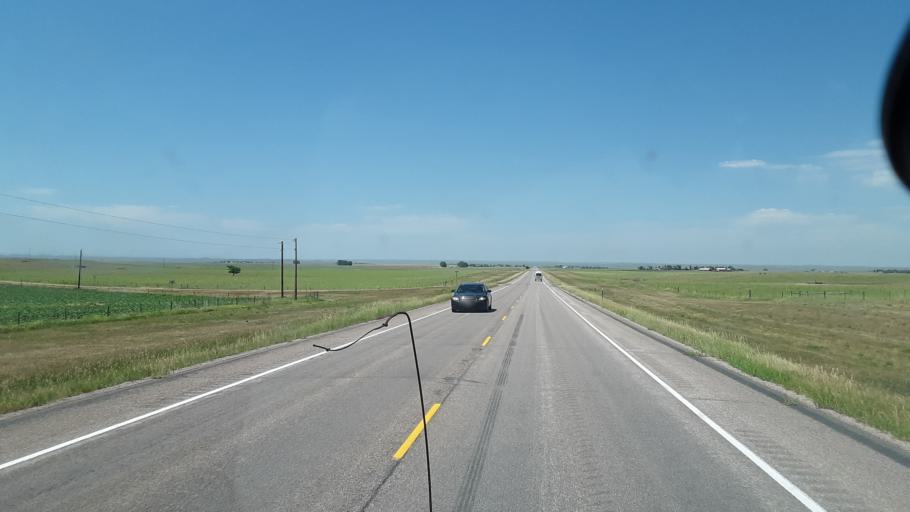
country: US
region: South Dakota
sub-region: Pennington County
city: Box Elder
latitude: 43.8358
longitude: -102.5886
